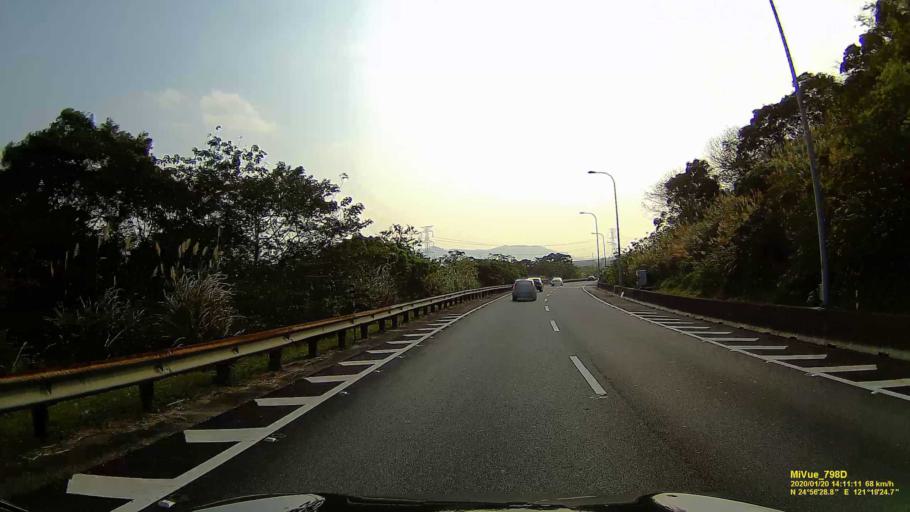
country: TW
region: Taiwan
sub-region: Taoyuan
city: Taoyuan
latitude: 24.9409
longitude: 121.3234
